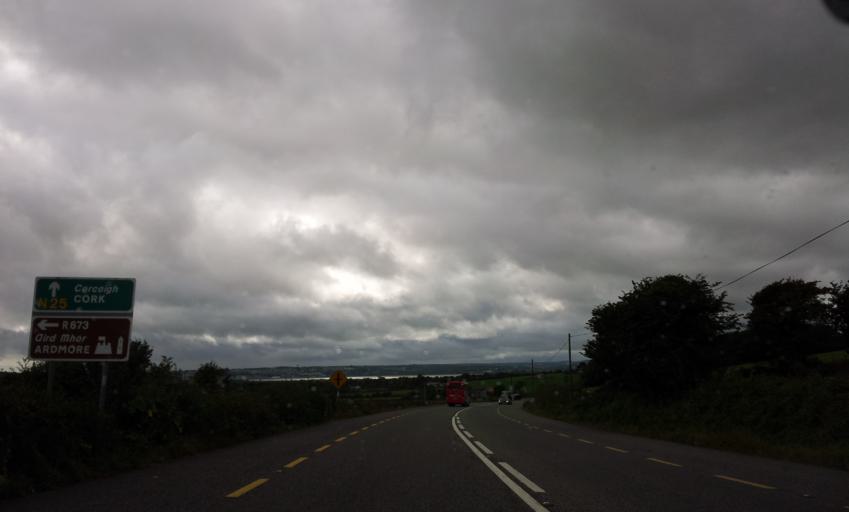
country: IE
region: Munster
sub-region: County Cork
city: Youghal
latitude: 51.9738
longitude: -7.7722
